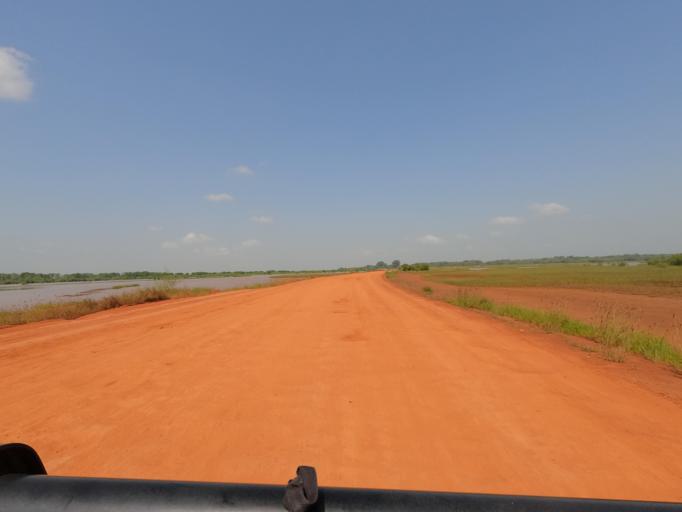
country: GW
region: Cacheu
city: Canchungo
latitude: 12.2563
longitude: -15.7795
